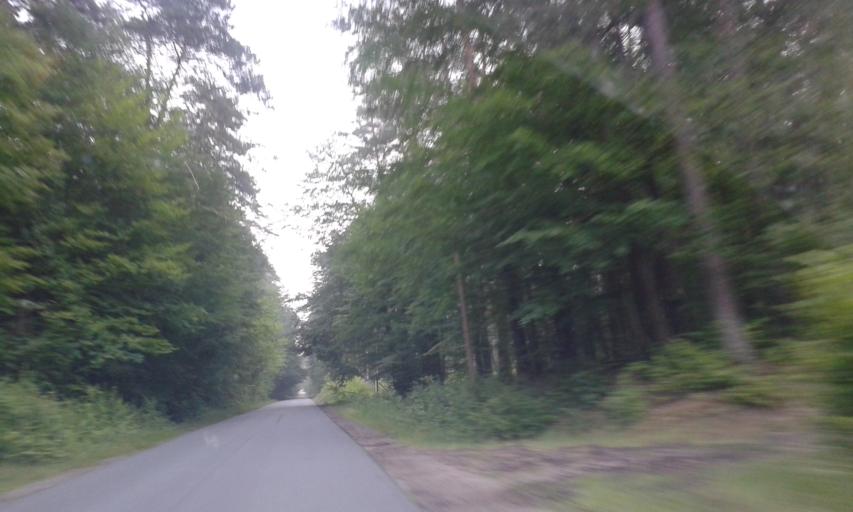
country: PL
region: Kujawsko-Pomorskie
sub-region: Powiat sepolenski
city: Sypniewo
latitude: 53.4514
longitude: 17.3681
